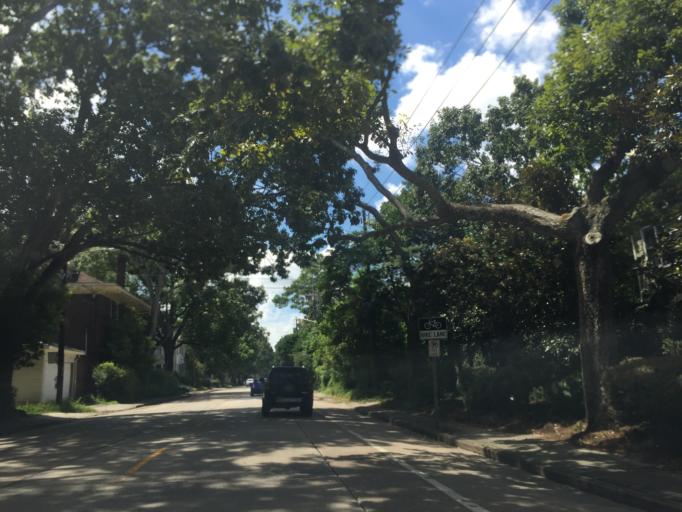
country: US
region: Georgia
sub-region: Chatham County
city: Savannah
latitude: 32.0506
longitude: -81.0977
